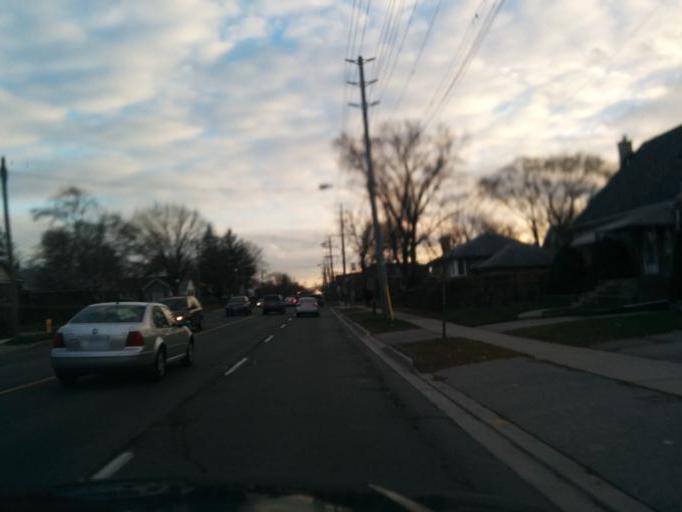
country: CA
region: Ontario
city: Etobicoke
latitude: 43.6423
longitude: -79.5224
